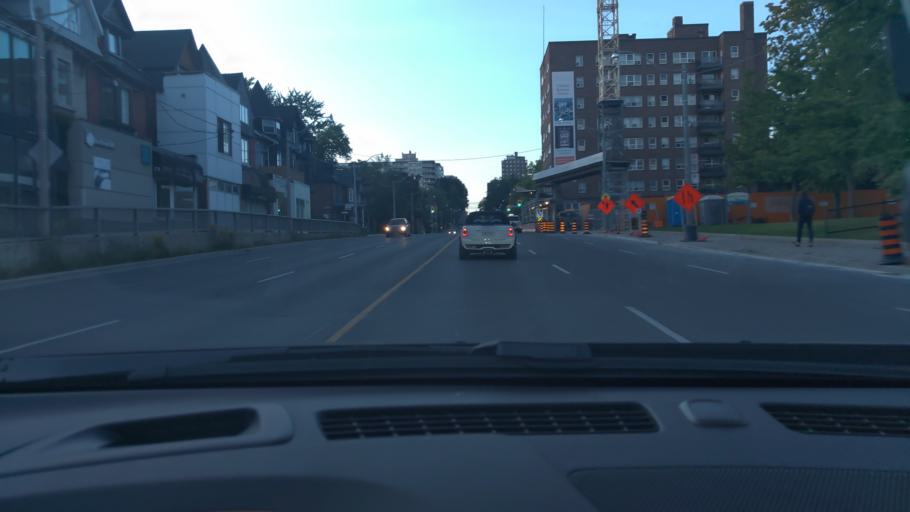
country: CA
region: Ontario
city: Toronto
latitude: 43.6783
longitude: -79.3980
